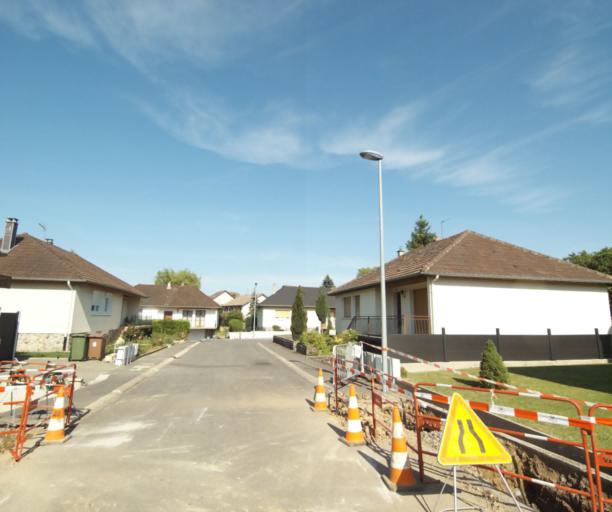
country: FR
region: Champagne-Ardenne
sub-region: Departement des Ardennes
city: Warcq
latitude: 49.7827
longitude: 4.6910
